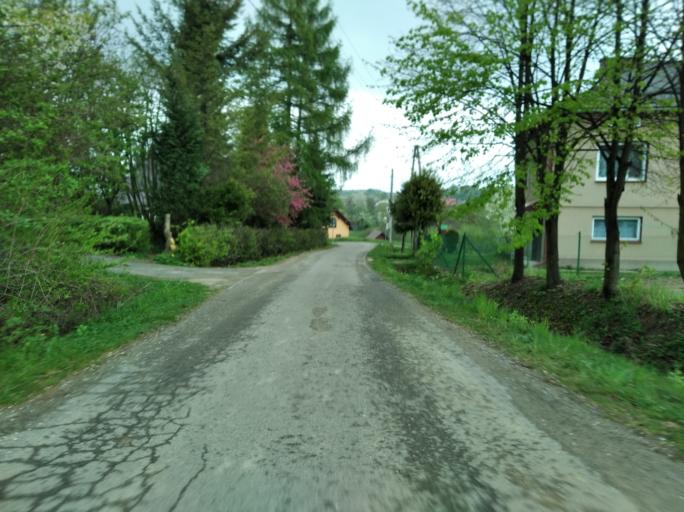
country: PL
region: Subcarpathian Voivodeship
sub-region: Powiat brzozowski
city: Golcowa
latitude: 49.7550
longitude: 22.0581
